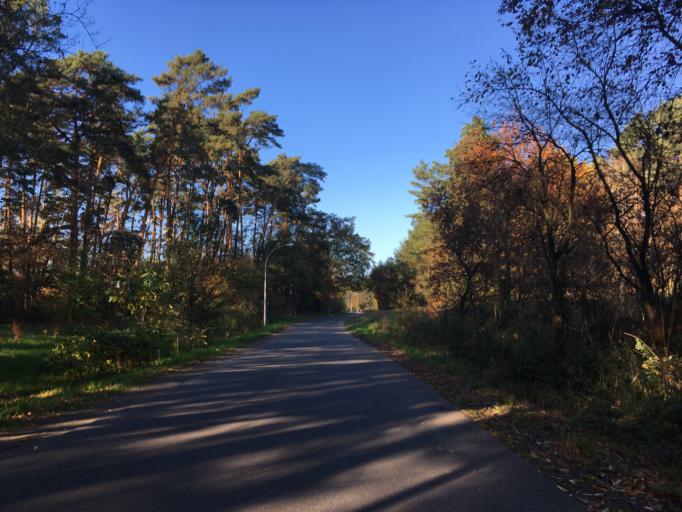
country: DE
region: Brandenburg
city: Reichenwalde
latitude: 52.2888
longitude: 14.0090
